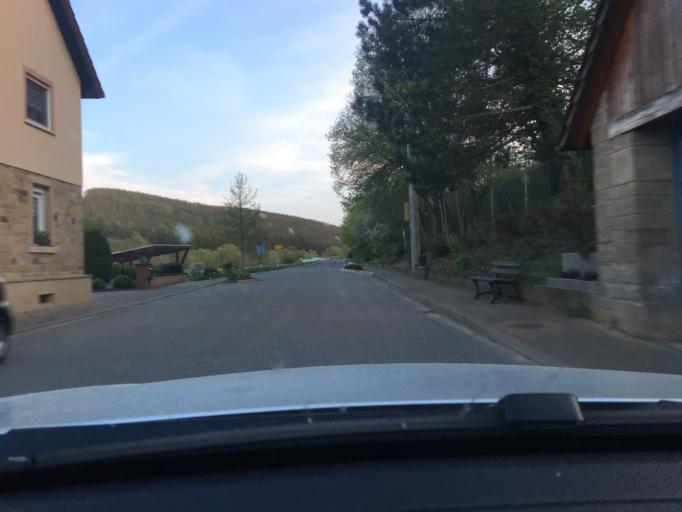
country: DE
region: Rheinland-Pfalz
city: Munsterappel
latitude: 49.7334
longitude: 7.8761
